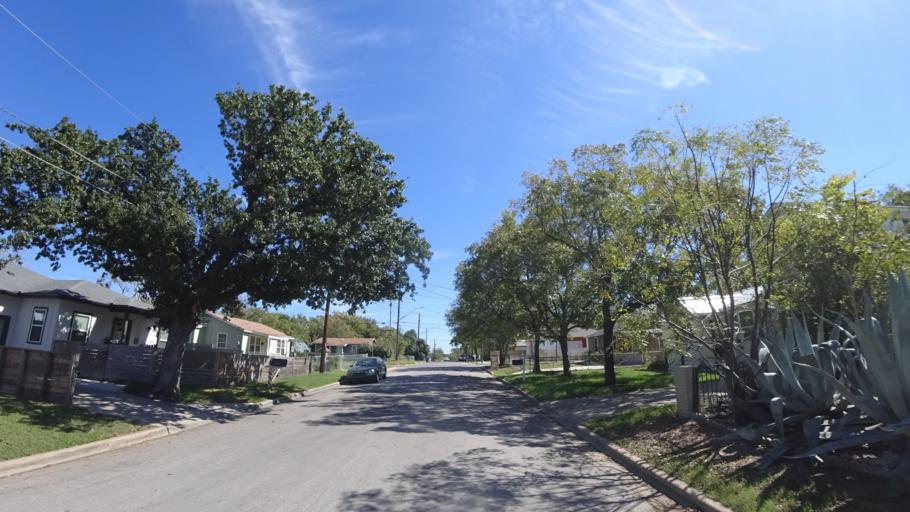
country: US
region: Texas
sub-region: Travis County
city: Austin
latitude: 30.2758
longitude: -97.6871
